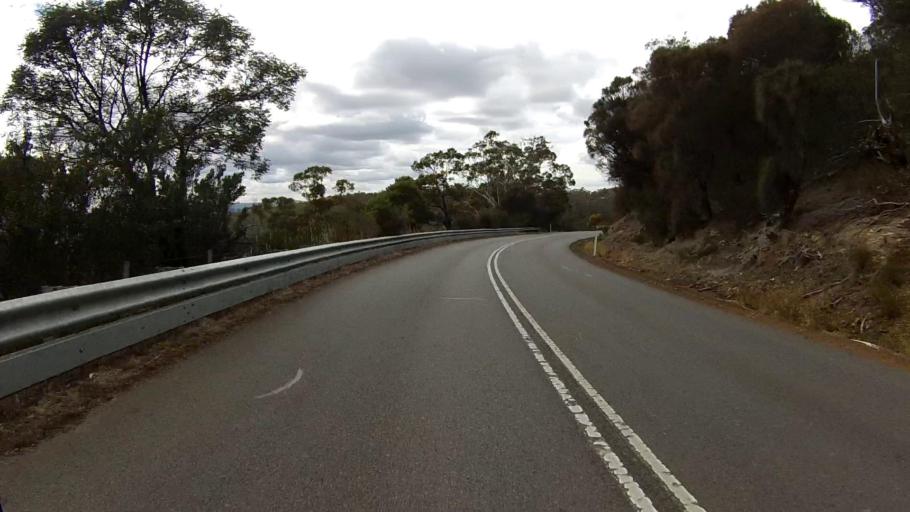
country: AU
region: Tasmania
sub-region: Clarence
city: Lindisfarne
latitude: -42.7791
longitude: 147.3687
